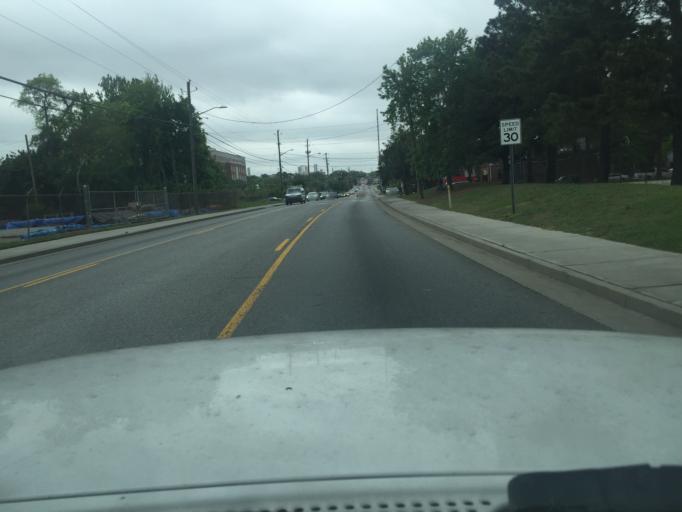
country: US
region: Georgia
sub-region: Chatham County
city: Savannah
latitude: 32.0679
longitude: -81.0810
